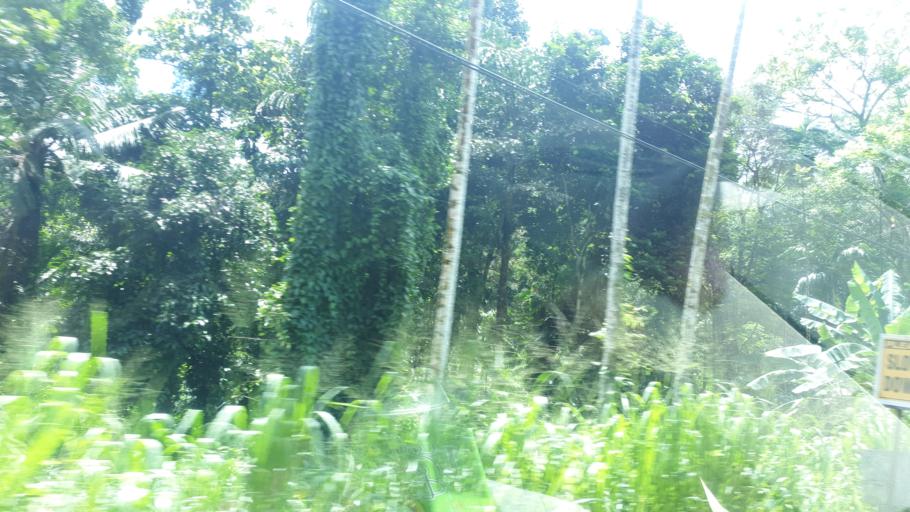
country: LK
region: Western
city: Horawala Junction
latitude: 6.5242
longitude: 80.2099
